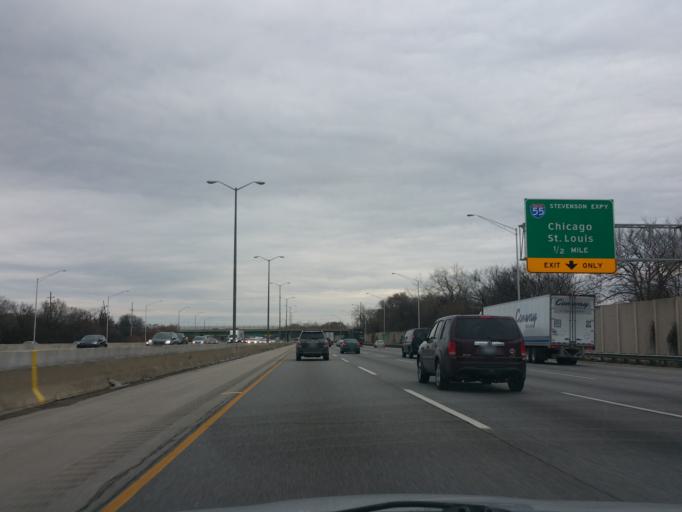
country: US
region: Illinois
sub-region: Cook County
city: Indian Head Park
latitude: 41.7785
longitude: -87.9079
